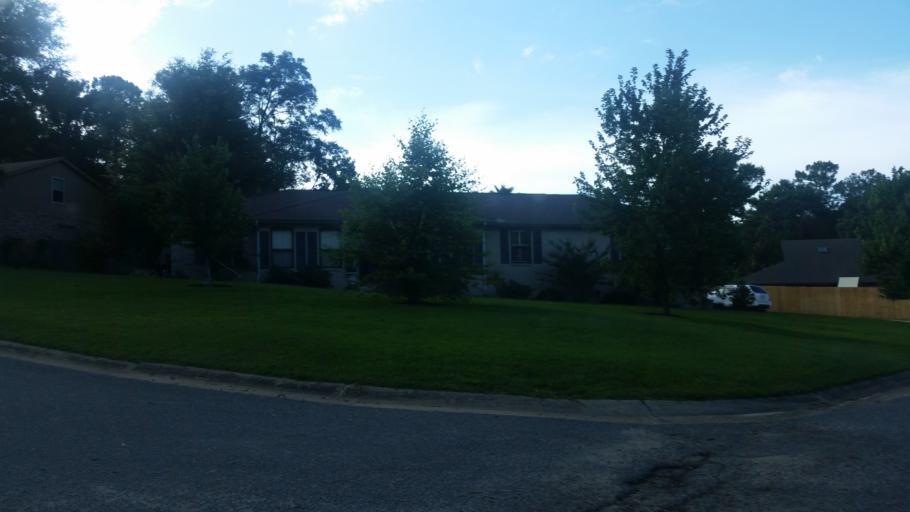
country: US
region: Florida
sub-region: Escambia County
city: Ferry Pass
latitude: 30.5103
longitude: -87.1671
